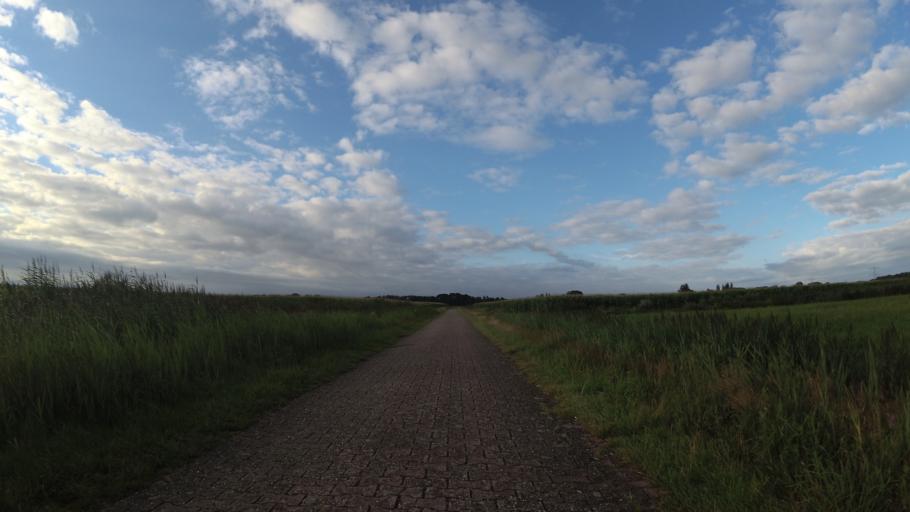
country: NL
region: North Brabant
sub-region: Gemeente Breda
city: Hoge Vucht
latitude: 51.6222
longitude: 4.7884
